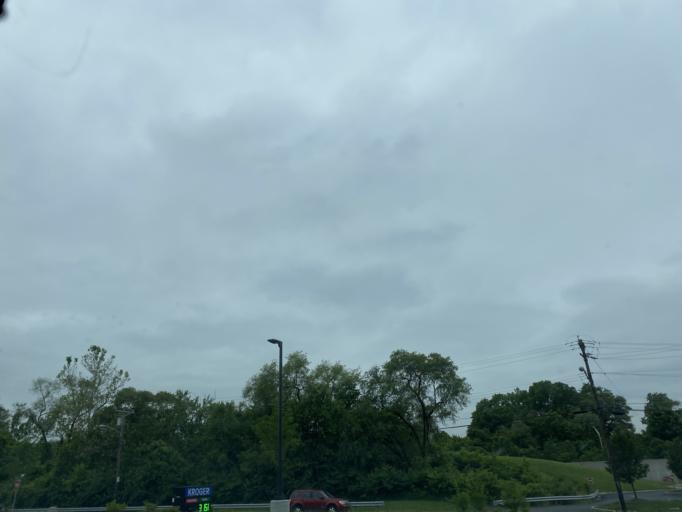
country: US
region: Kentucky
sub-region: Campbell County
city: Bellevue
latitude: 39.1001
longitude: -84.4861
